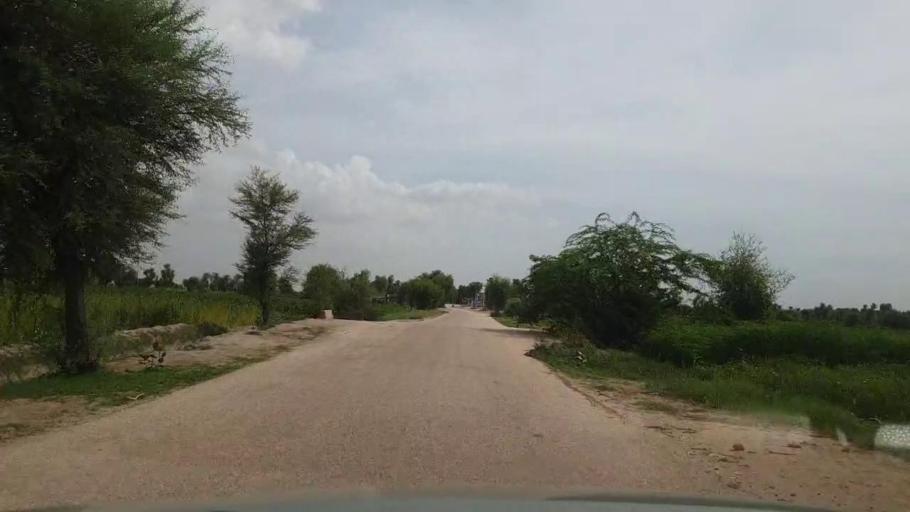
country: PK
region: Sindh
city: Kot Diji
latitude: 27.1379
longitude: 69.0281
